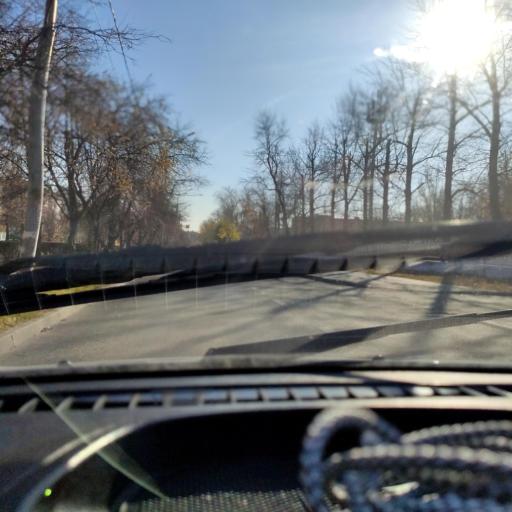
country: RU
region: Samara
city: Tol'yatti
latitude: 53.5039
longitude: 49.4131
